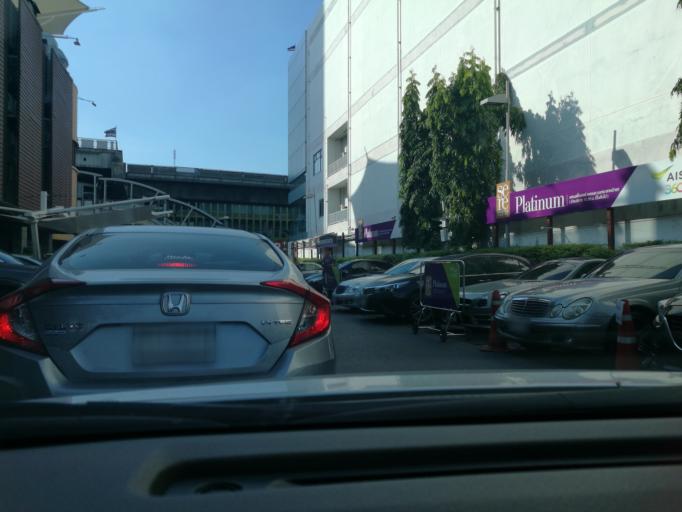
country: TH
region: Bangkok
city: Phaya Thai
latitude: 13.7803
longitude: 100.5457
